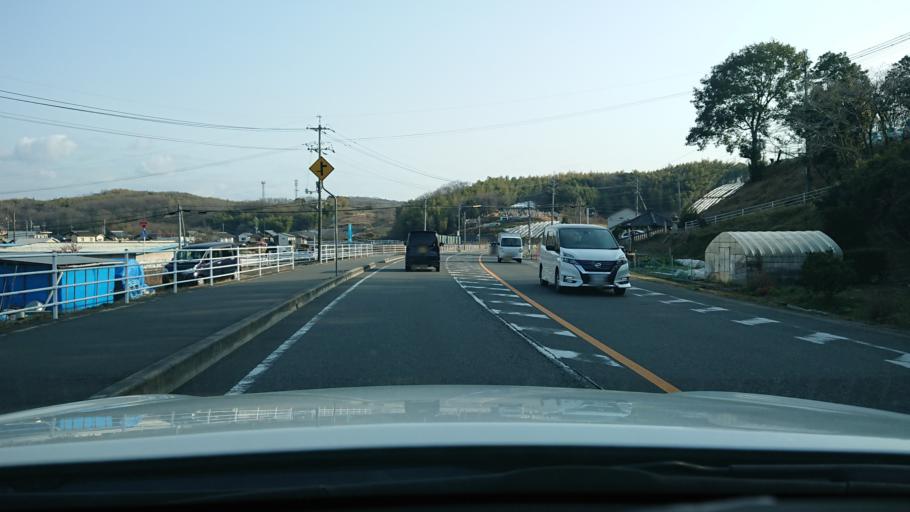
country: JP
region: Okayama
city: Kurashiki
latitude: 34.6065
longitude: 133.7080
